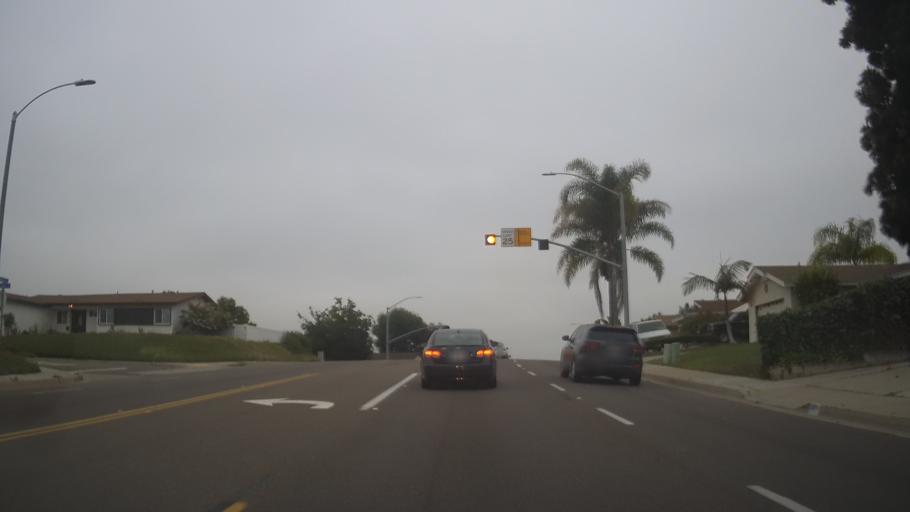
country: US
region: California
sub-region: San Diego County
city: Bonita
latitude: 32.6277
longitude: -117.0476
